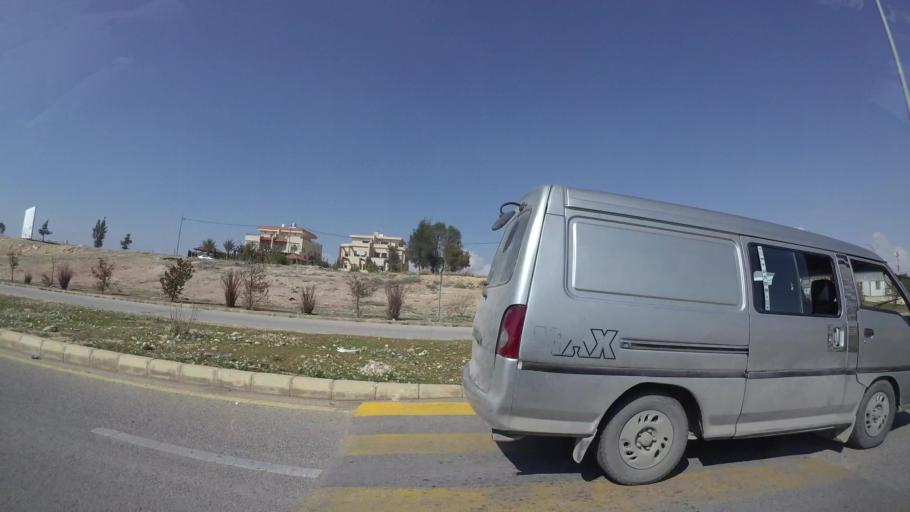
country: JO
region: Zarqa
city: Zarqa
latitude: 32.0730
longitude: 36.1064
